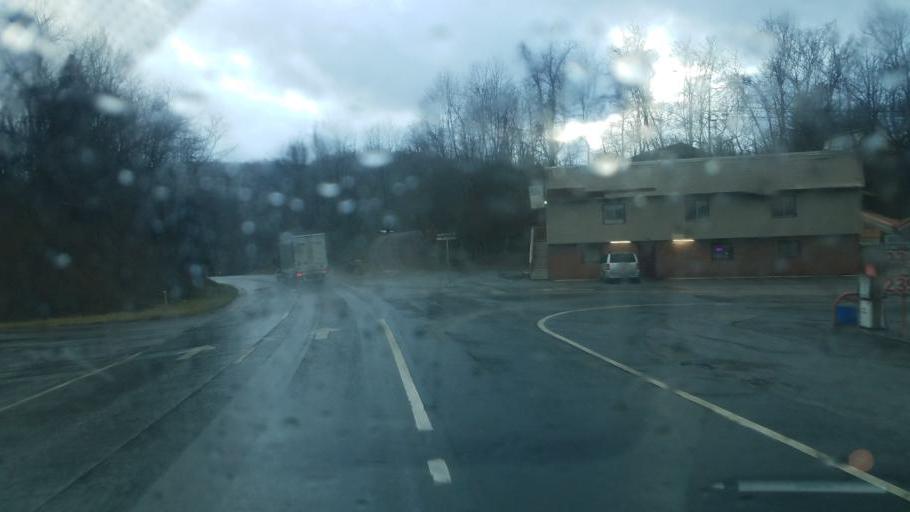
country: US
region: Virginia
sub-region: Giles County
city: Pearisburg
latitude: 37.2911
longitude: -80.7418
